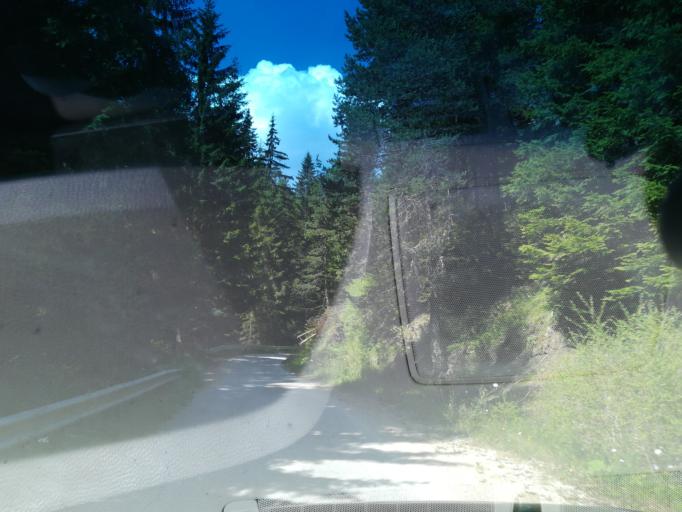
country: BG
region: Smolyan
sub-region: Obshtina Chepelare
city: Chepelare
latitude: 41.6701
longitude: 24.7952
